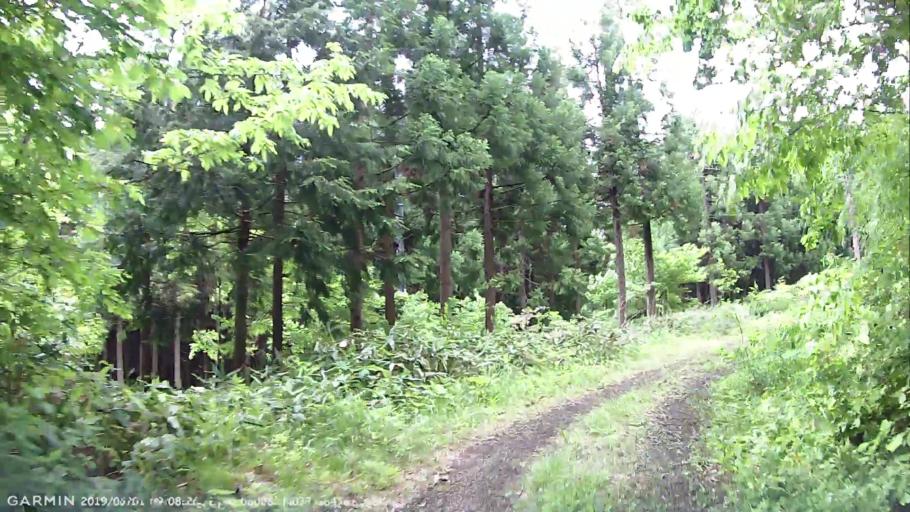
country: JP
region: Fukushima
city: Inawashiro
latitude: 37.3844
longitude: 140.0610
